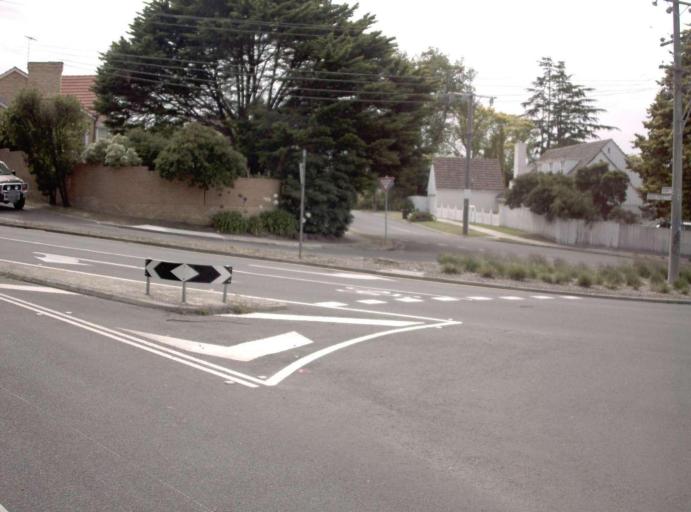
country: AU
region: Victoria
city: Ivanhoe East
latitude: -37.7703
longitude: 145.0634
